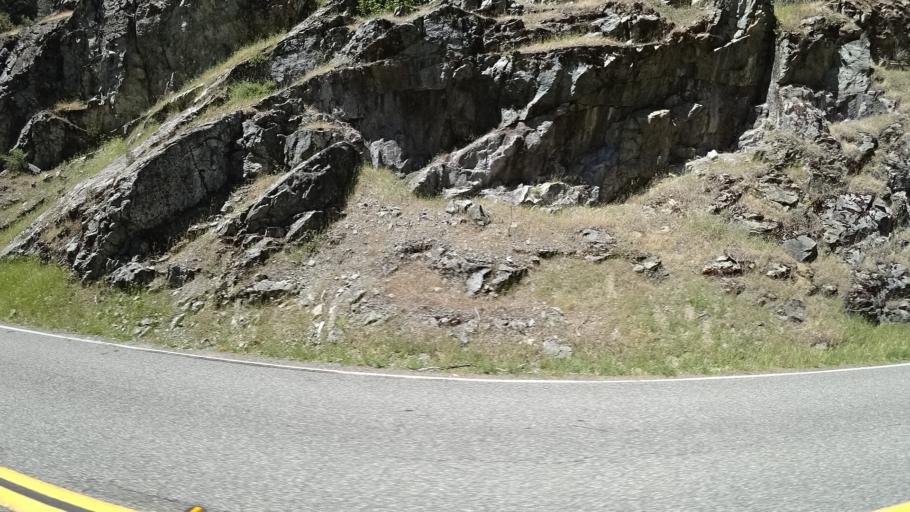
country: US
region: California
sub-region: Trinity County
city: Hayfork
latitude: 40.7485
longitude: -123.1698
